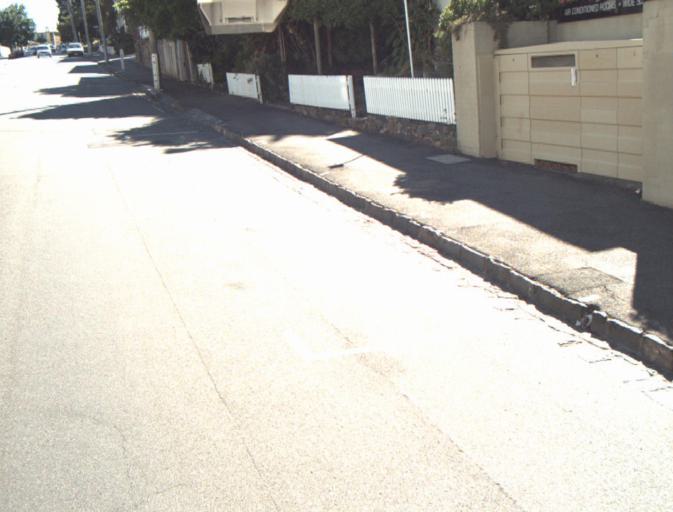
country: AU
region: Tasmania
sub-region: Launceston
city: Launceston
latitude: -41.4367
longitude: 147.1426
